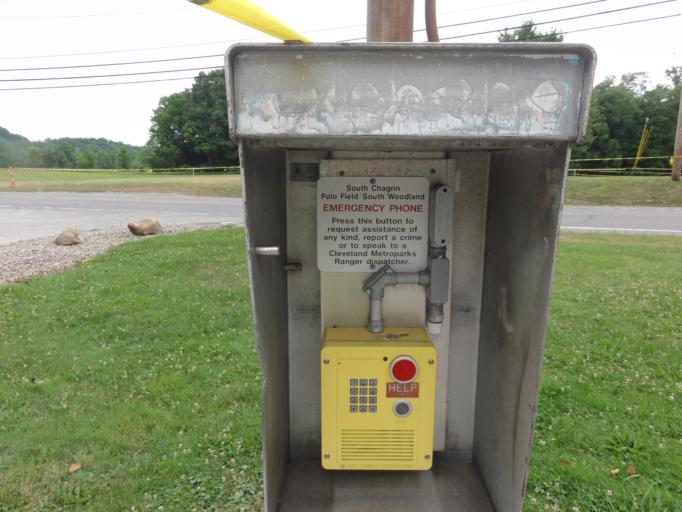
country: US
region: Ohio
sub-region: Cuyahoga County
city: Moreland Hills
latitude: 41.4582
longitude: -81.4065
